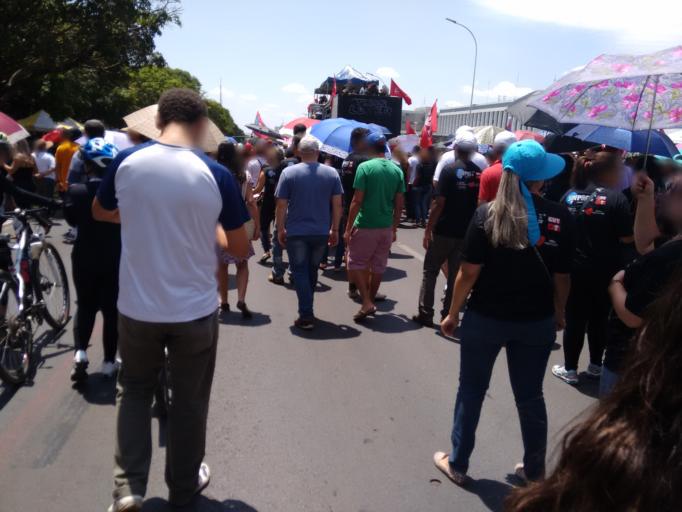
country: BR
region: Federal District
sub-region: Brasilia
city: Brasilia
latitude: -15.7857
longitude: -47.9114
